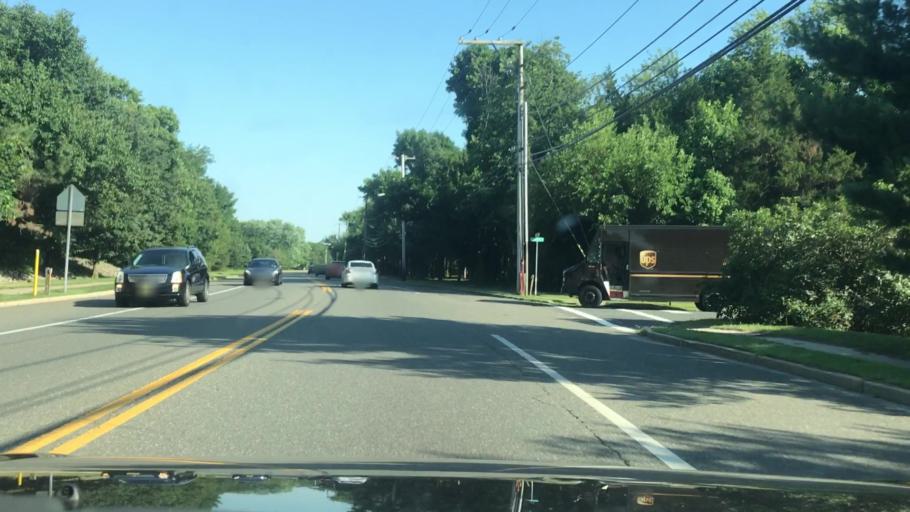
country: US
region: New Jersey
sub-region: Ocean County
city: Silver Ridge
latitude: 39.9997
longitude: -74.1996
